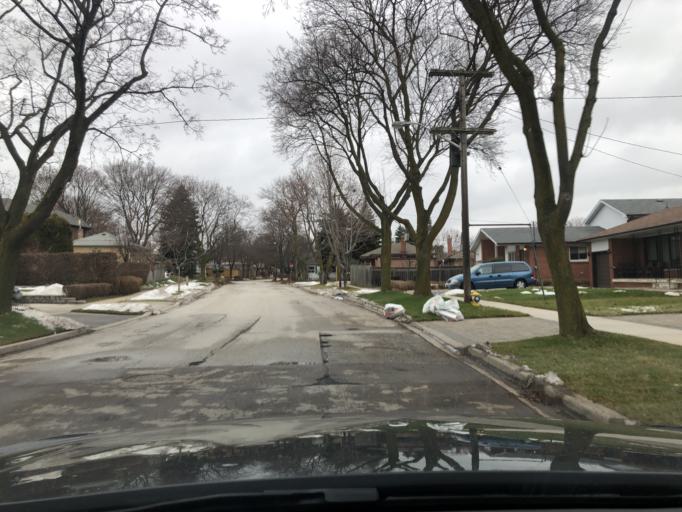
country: CA
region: Ontario
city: Etobicoke
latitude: 43.6928
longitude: -79.5203
